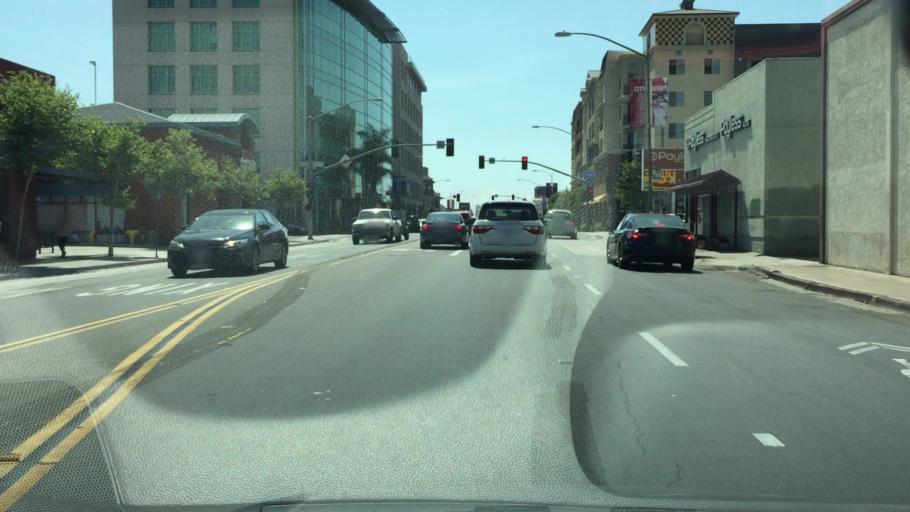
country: US
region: California
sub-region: San Diego County
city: San Diego
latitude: 32.7497
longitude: -117.1001
